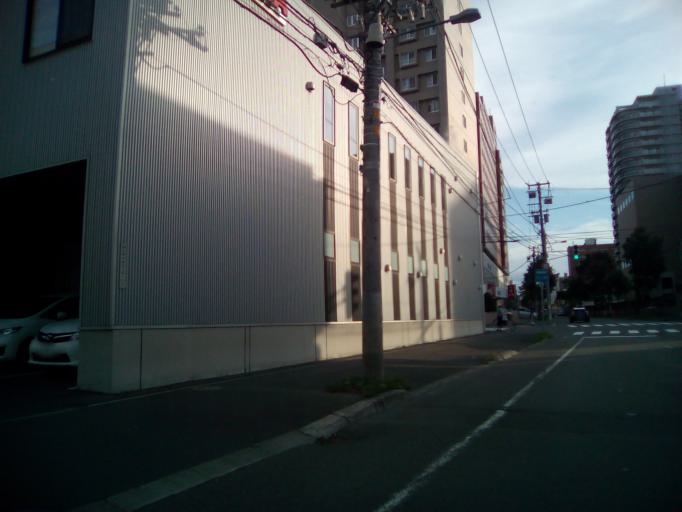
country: JP
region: Hokkaido
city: Sapporo
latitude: 43.0542
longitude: 141.3857
